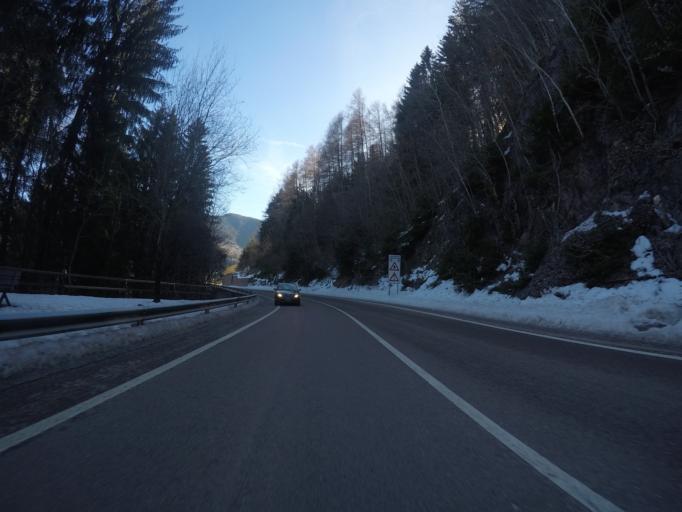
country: IT
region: Trentino-Alto Adige
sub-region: Provincia di Trento
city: Capriana
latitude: 46.2637
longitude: 11.3428
